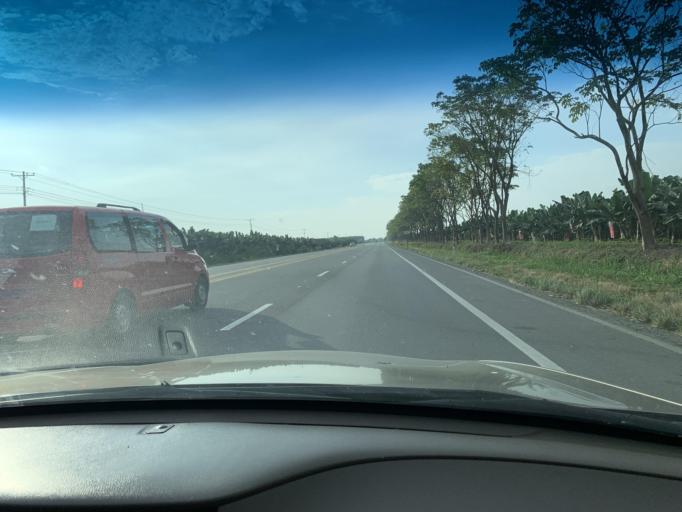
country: EC
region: Guayas
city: Coronel Marcelino Mariduena
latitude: -2.2699
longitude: -79.5407
